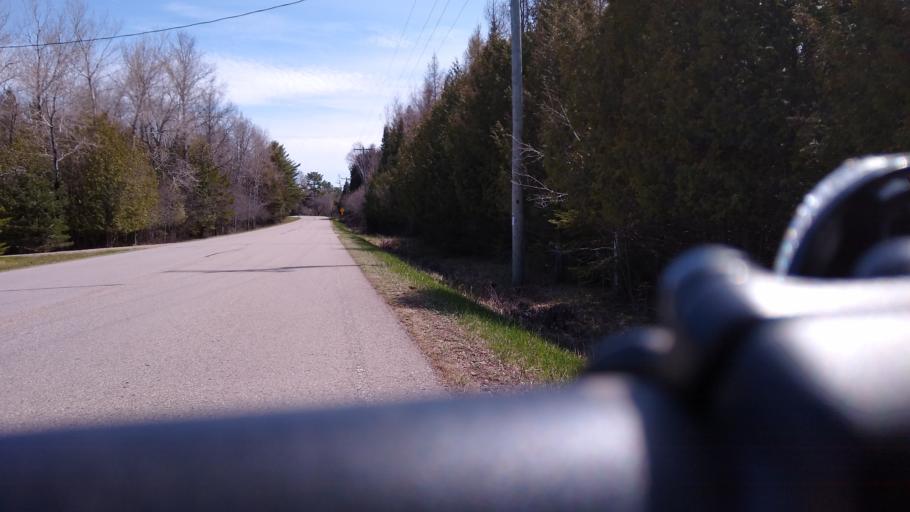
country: US
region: Michigan
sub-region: Delta County
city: Escanaba
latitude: 45.6905
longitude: -87.1526
